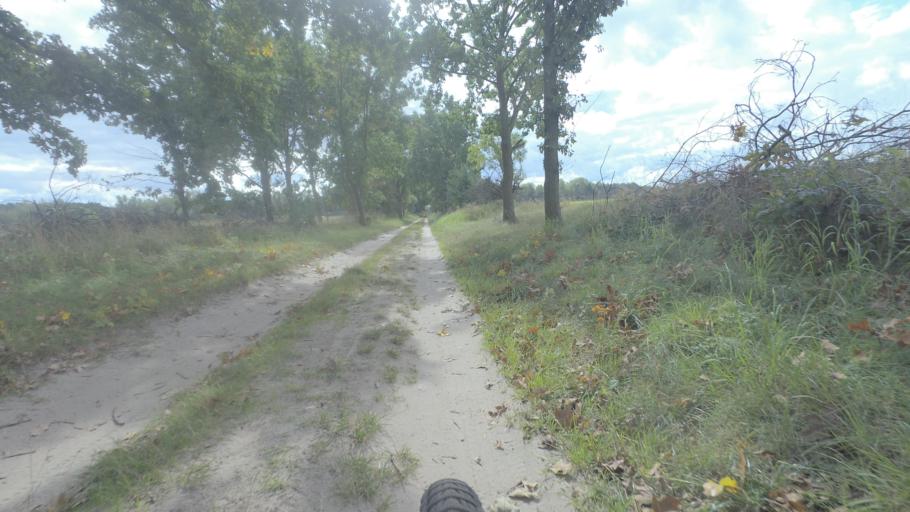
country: DE
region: Brandenburg
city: Ludwigsfelde
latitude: 52.3222
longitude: 13.2059
